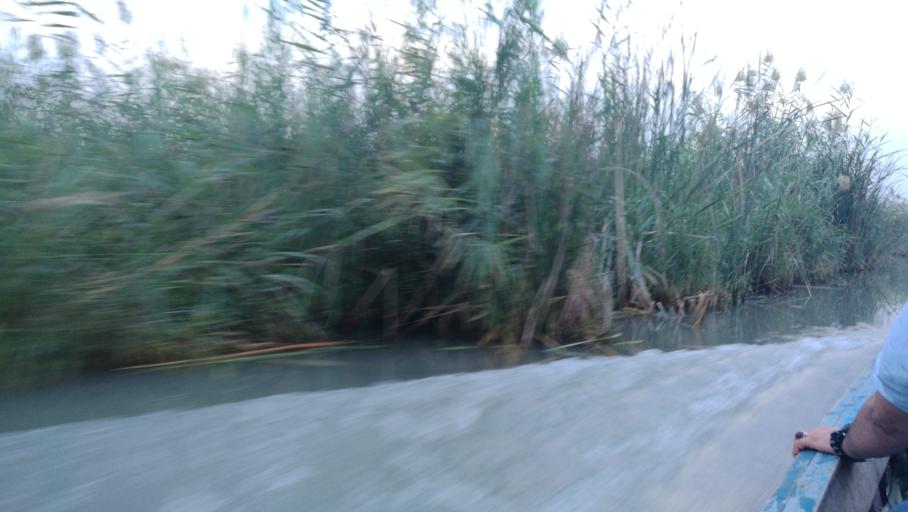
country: IQ
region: Dhi Qar
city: Al Jabayish
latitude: 30.9880
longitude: 47.0445
